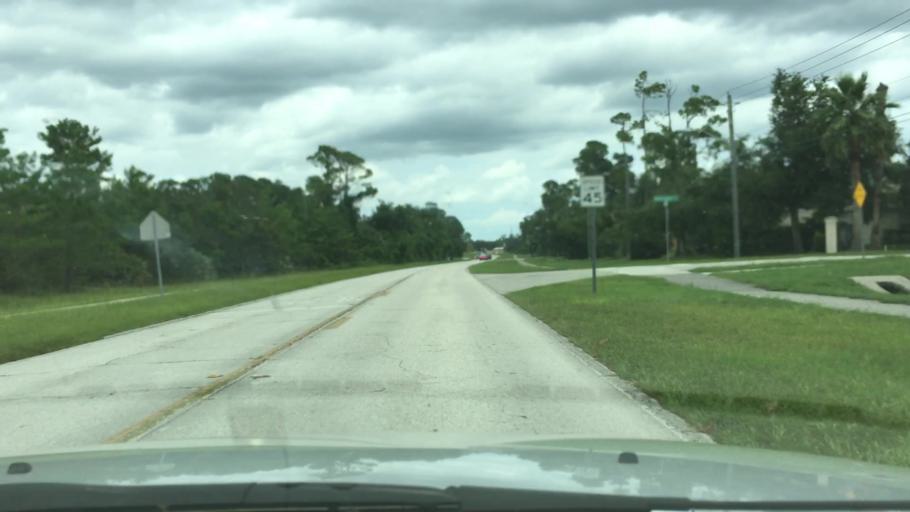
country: US
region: Florida
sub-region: Volusia County
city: Holly Hill
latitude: 29.2261
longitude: -81.0704
